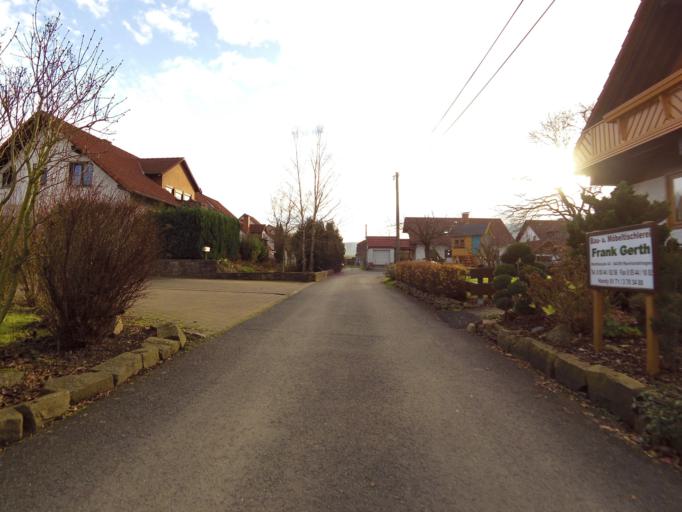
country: DE
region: Lower Saxony
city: Buhren
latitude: 51.4886
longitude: 9.6044
